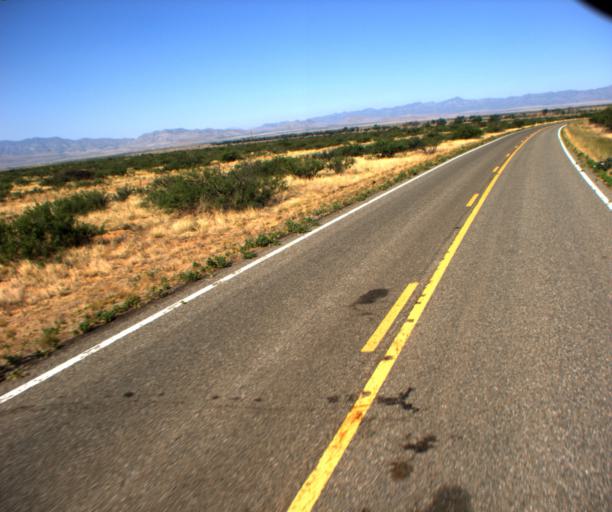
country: US
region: Arizona
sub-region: Graham County
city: Swift Trail Junction
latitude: 32.5824
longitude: -109.9484
